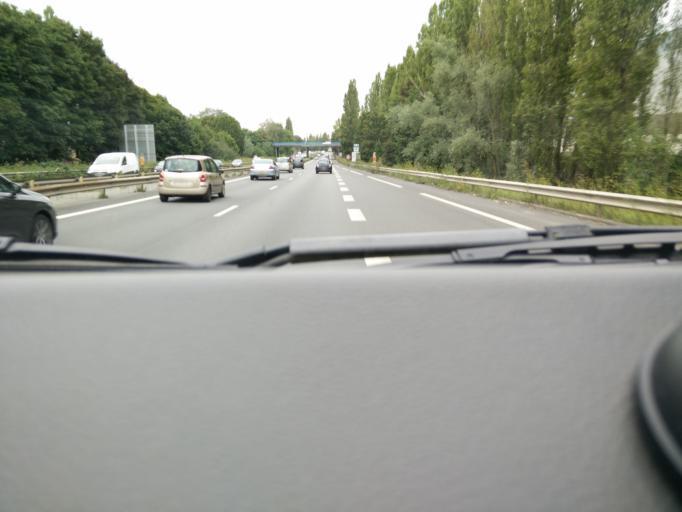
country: FR
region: Nord-Pas-de-Calais
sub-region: Departement du Nord
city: Petite-Foret
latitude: 50.3614
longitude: 3.4856
